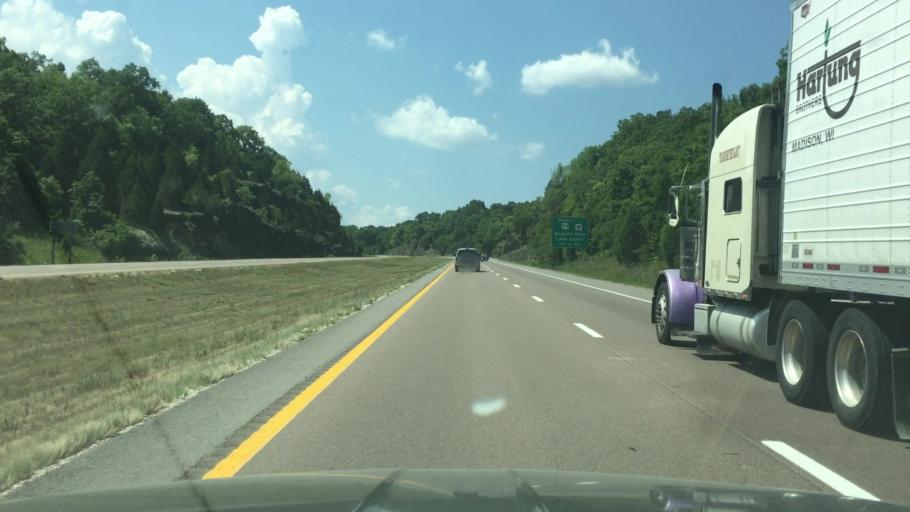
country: US
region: Missouri
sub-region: Miller County
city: Lake Ozark
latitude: 38.2267
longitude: -92.6245
